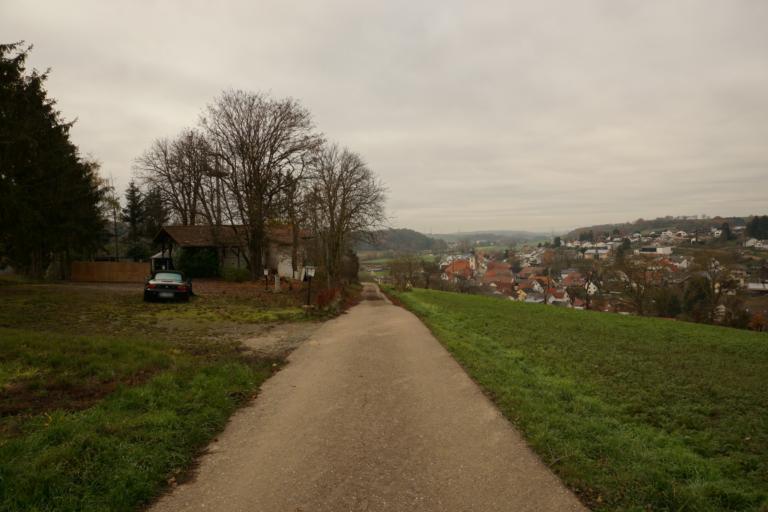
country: DE
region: Baden-Wuerttemberg
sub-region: Karlsruhe Region
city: Huffenhardt
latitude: 49.3043
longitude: 9.0285
